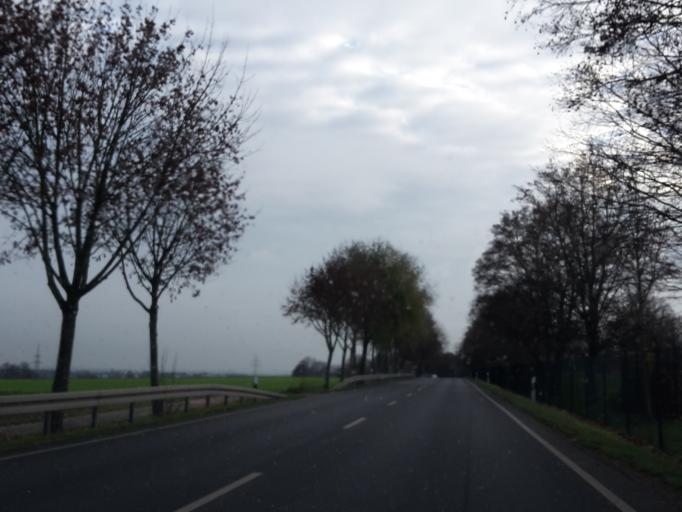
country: DE
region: Hesse
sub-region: Regierungsbezirk Darmstadt
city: Wiesbaden
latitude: 50.0756
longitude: 8.2722
